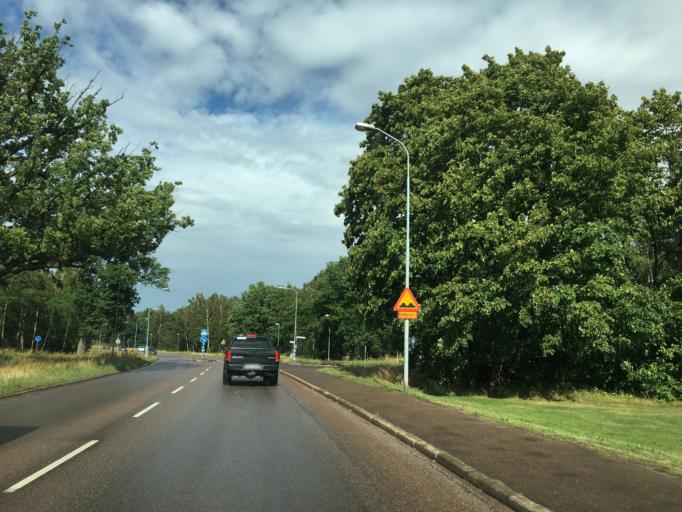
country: SE
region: Kalmar
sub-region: Kalmar Kommun
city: Kalmar
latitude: 56.6974
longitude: 16.3375
